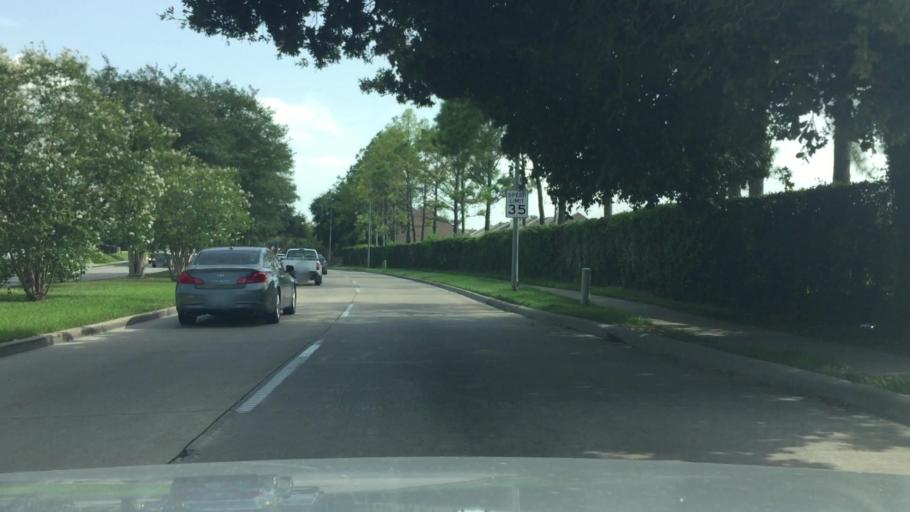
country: US
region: Texas
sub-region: Harris County
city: Bunker Hill Village
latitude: 29.7610
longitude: -95.5764
